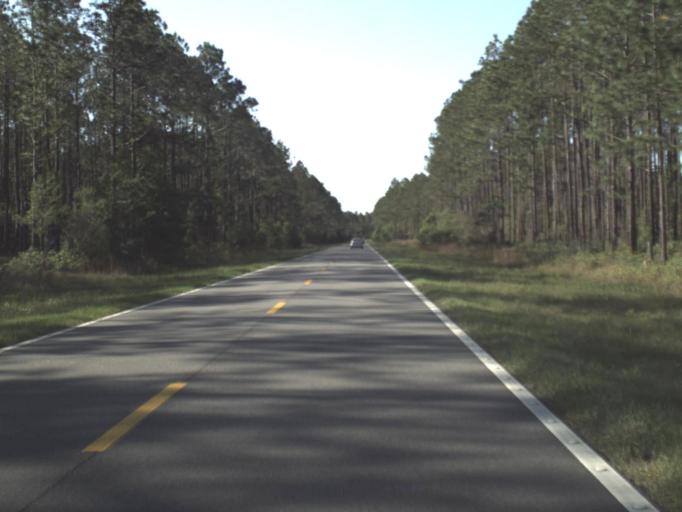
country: US
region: Florida
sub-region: Gulf County
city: Wewahitchka
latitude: 30.1224
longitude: -84.9886
